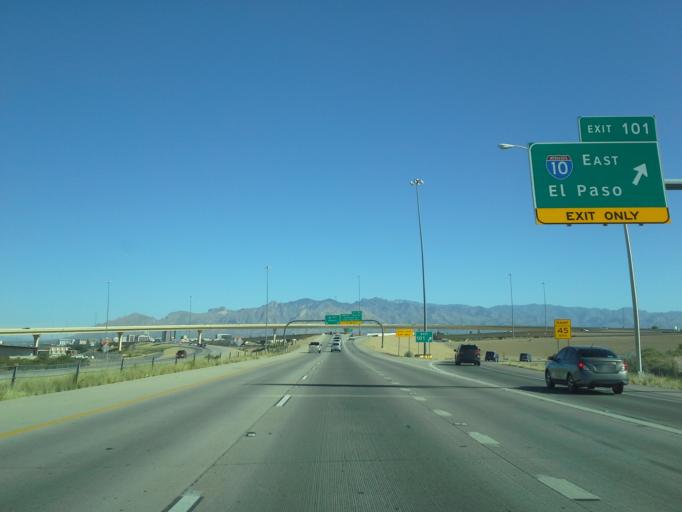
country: US
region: Arizona
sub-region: Pima County
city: South Tucson
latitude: 32.1910
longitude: -110.9806
